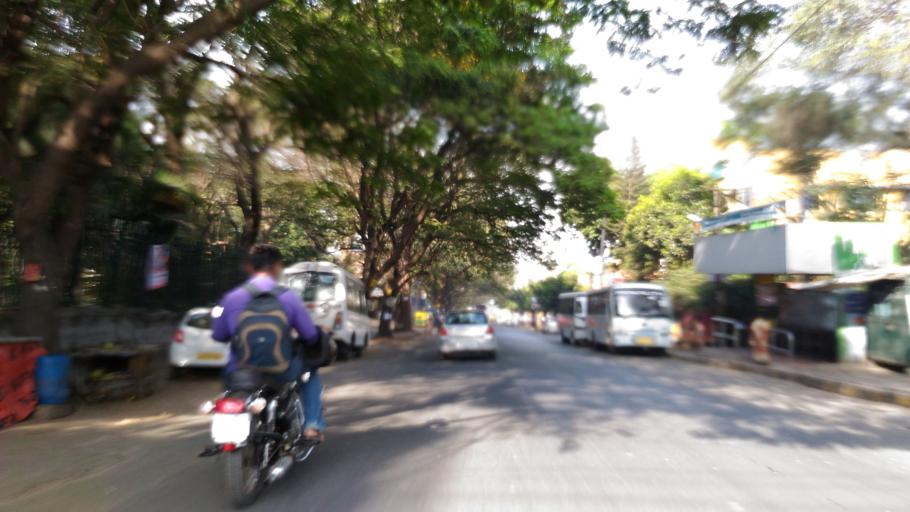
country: IN
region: Karnataka
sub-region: Bangalore Urban
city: Bangalore
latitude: 12.9433
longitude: 77.5433
